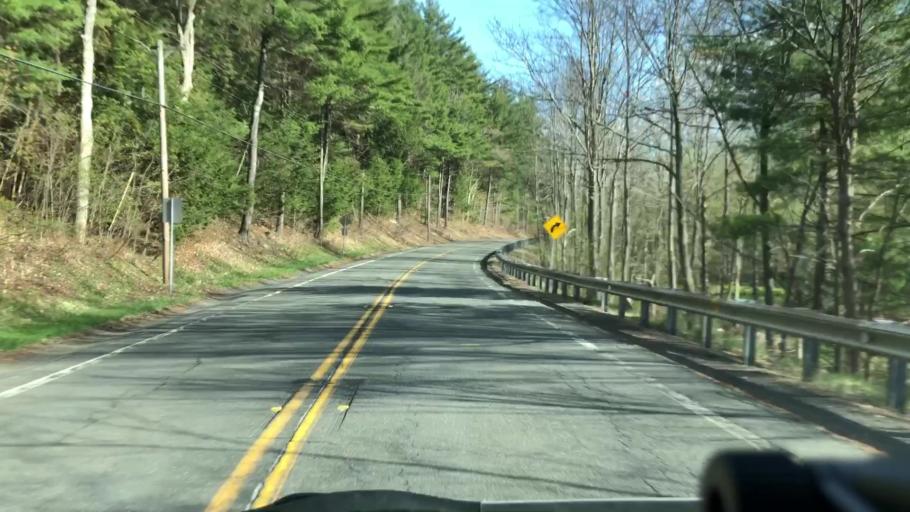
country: US
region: Massachusetts
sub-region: Hampshire County
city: Chesterfield
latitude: 42.3658
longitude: -72.9088
